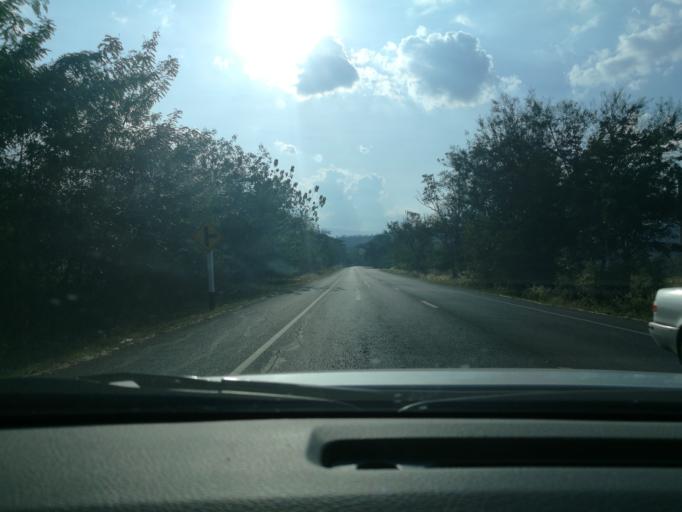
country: TH
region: Phetchabun
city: Phetchabun
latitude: 16.5477
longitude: 101.1241
